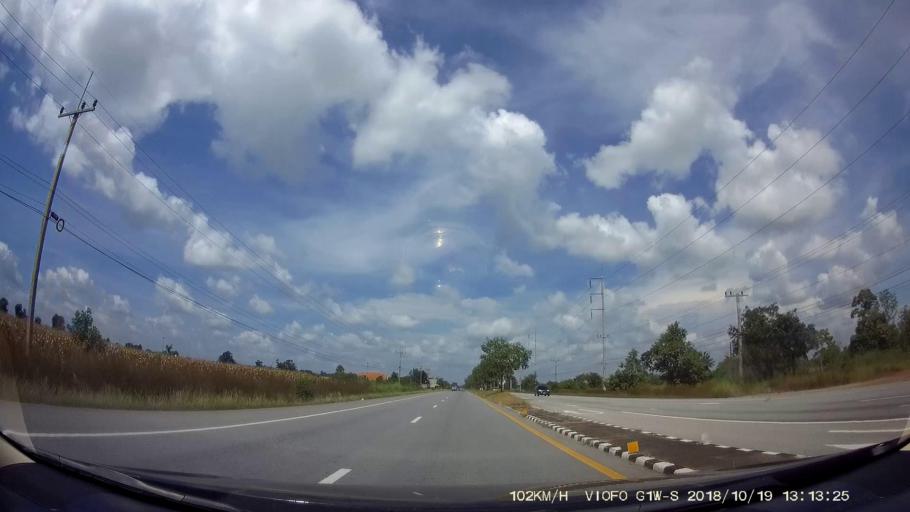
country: TH
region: Nakhon Ratchasima
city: Dan Khun Thot
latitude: 15.3596
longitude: 101.8294
